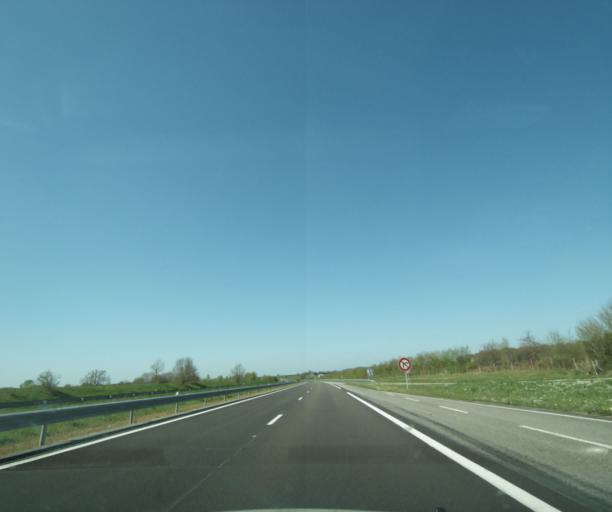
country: FR
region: Bourgogne
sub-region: Departement de la Nievre
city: Neuvy-sur-Loire
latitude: 47.5119
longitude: 2.9190
